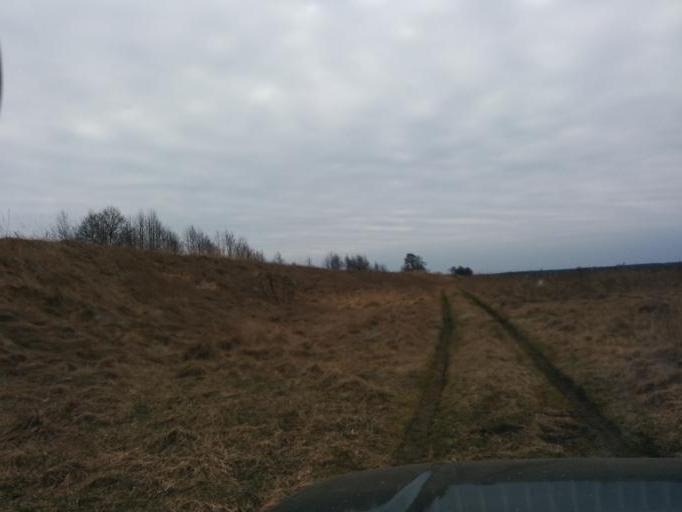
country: LV
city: Tireli
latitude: 56.9095
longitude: 23.6259
